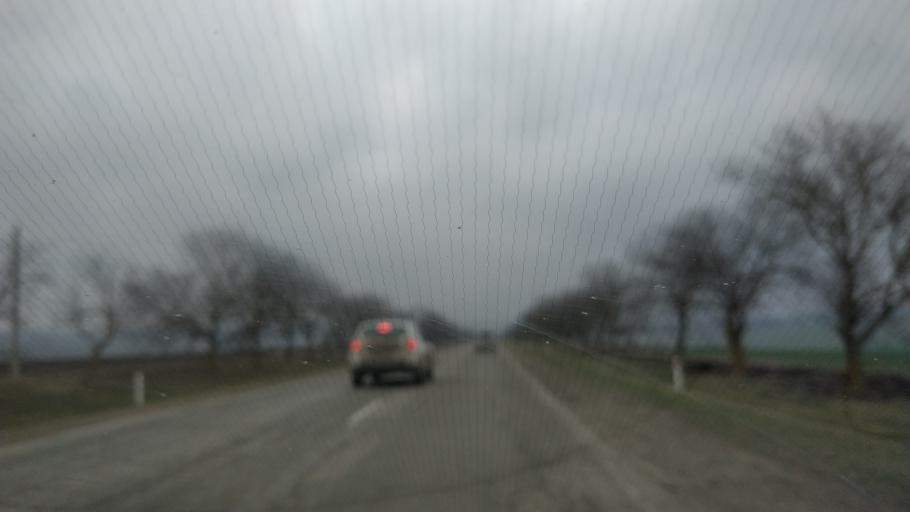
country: MD
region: Gagauzia
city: Comrat
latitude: 46.2560
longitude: 28.7538
